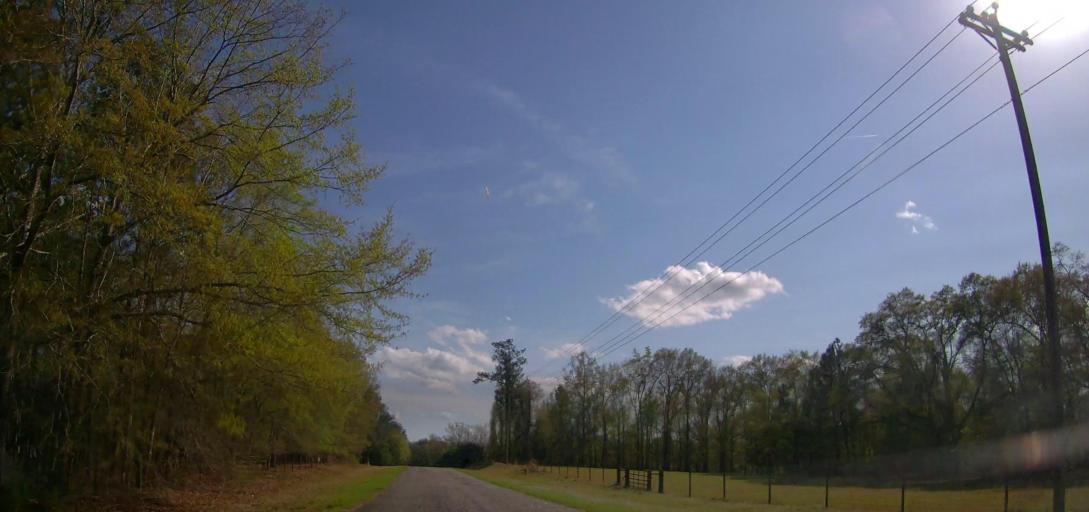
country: US
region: Georgia
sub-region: Baldwin County
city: Hardwick
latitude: 33.0322
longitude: -83.1191
